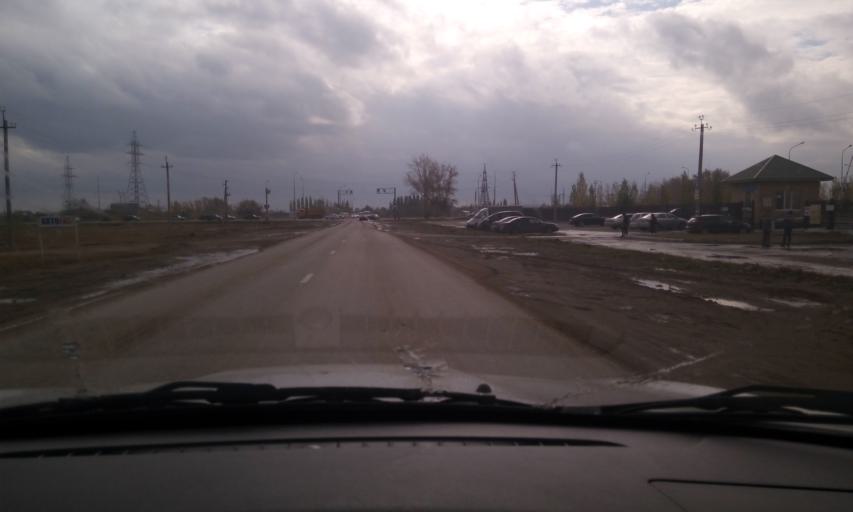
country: KZ
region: Astana Qalasy
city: Astana
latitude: 51.1399
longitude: 71.5299
